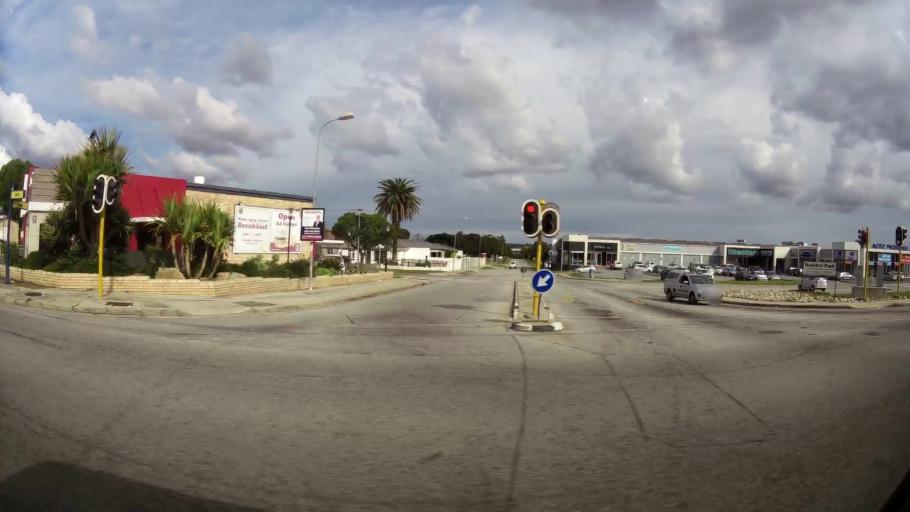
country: ZA
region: Eastern Cape
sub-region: Nelson Mandela Bay Metropolitan Municipality
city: Port Elizabeth
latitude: -33.9481
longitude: 25.5584
